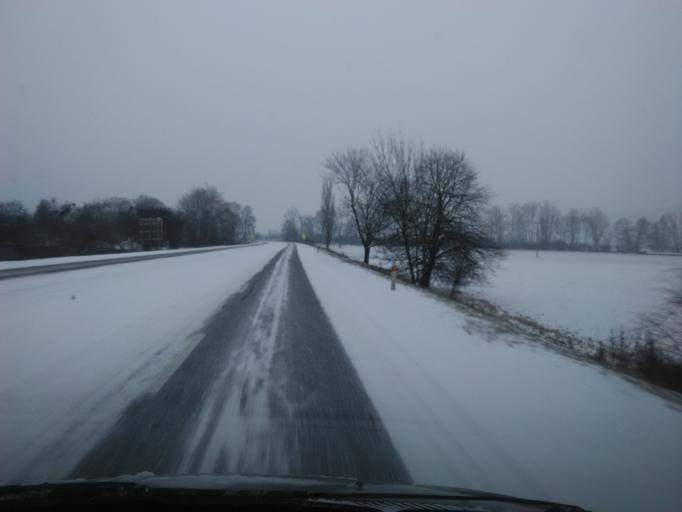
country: CZ
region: Olomoucky
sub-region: Okres Prerov
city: Hranice
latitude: 49.5468
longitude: 17.6868
